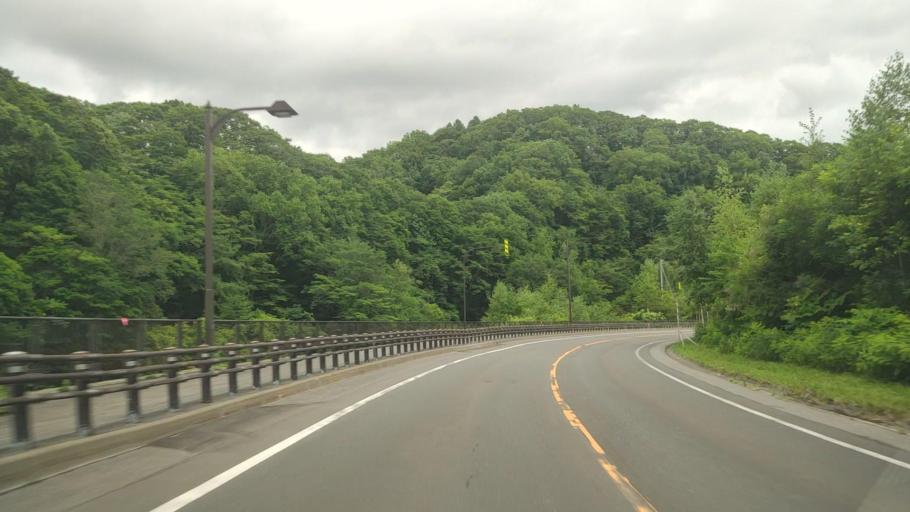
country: JP
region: Hokkaido
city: Date
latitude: 42.6177
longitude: 141.0242
